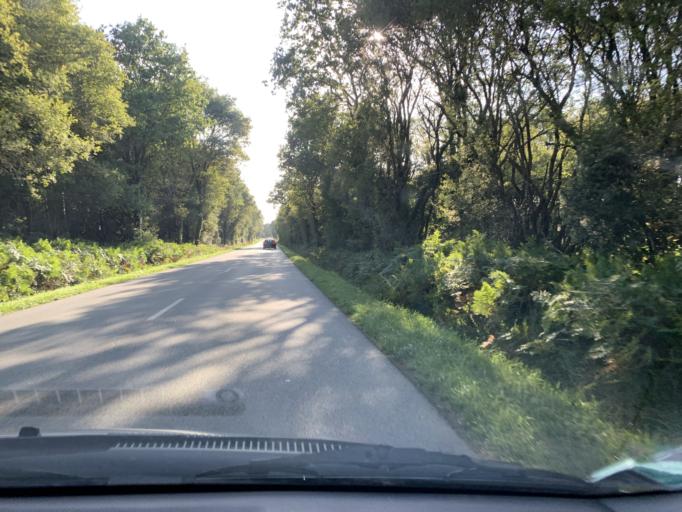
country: FR
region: Brittany
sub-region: Departement du Morbihan
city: Surzur
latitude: 47.5660
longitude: -2.6755
